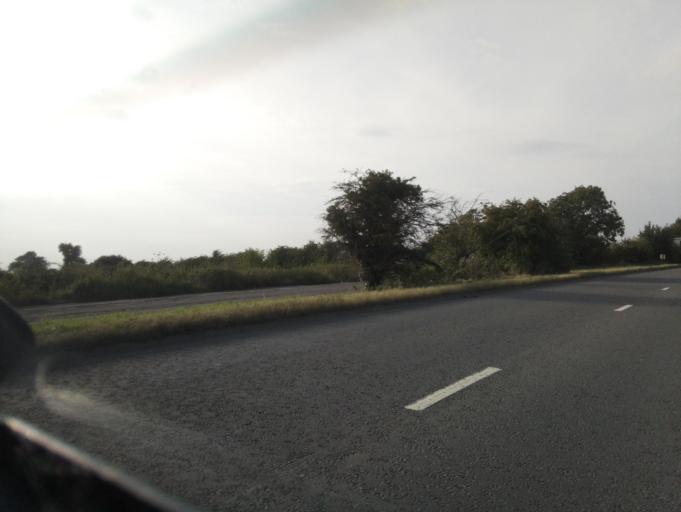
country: GB
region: England
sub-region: Gloucestershire
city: Gotherington
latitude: 51.9600
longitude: -2.0684
